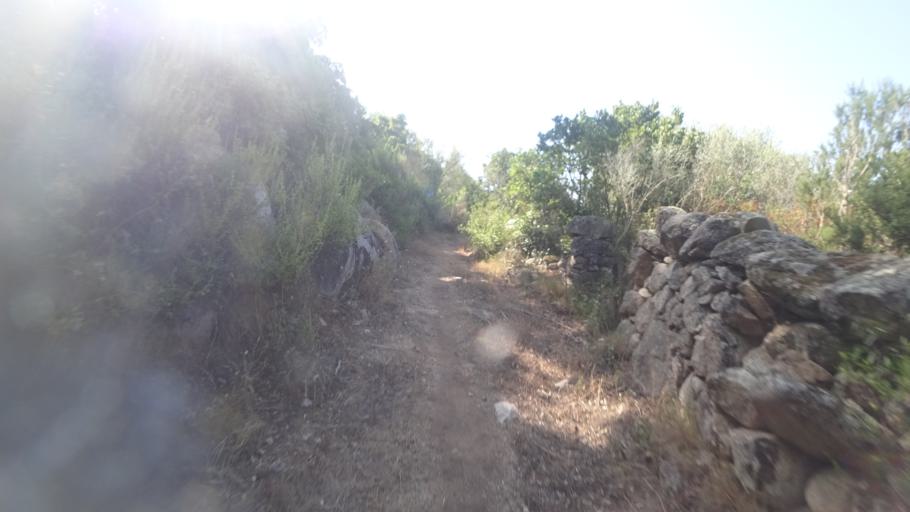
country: FR
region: Corsica
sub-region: Departement de la Corse-du-Sud
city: Porto-Vecchio
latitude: 41.6639
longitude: 9.3272
